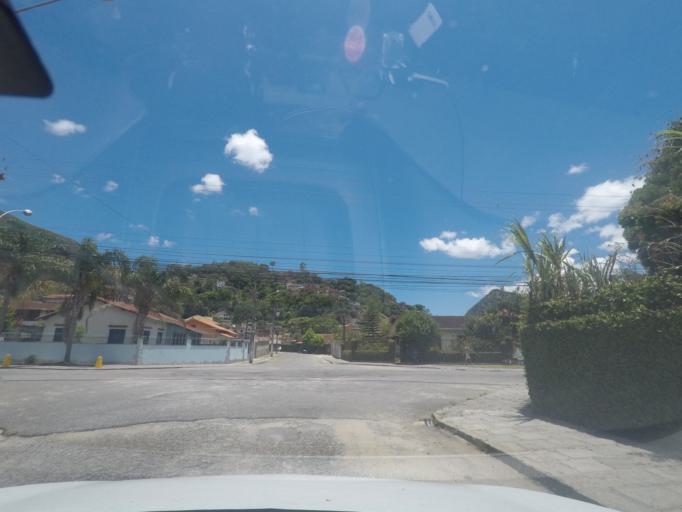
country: BR
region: Rio de Janeiro
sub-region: Teresopolis
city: Teresopolis
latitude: -22.4341
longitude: -42.9731
